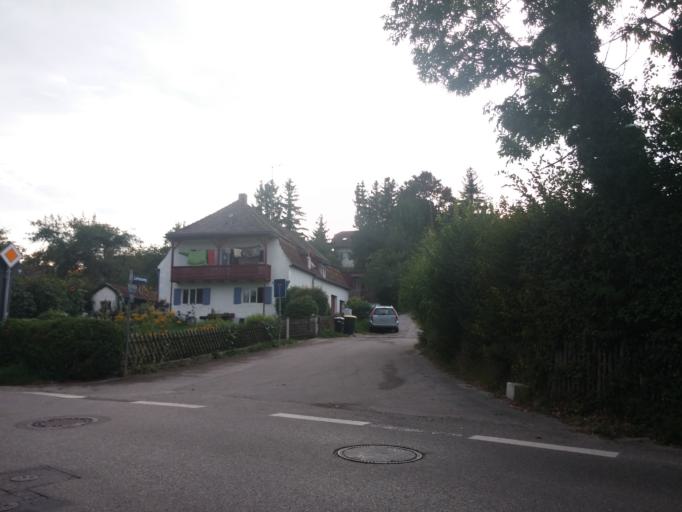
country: DE
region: Bavaria
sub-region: Upper Bavaria
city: Schondorf am Ammersee
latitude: 48.0532
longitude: 11.0878
